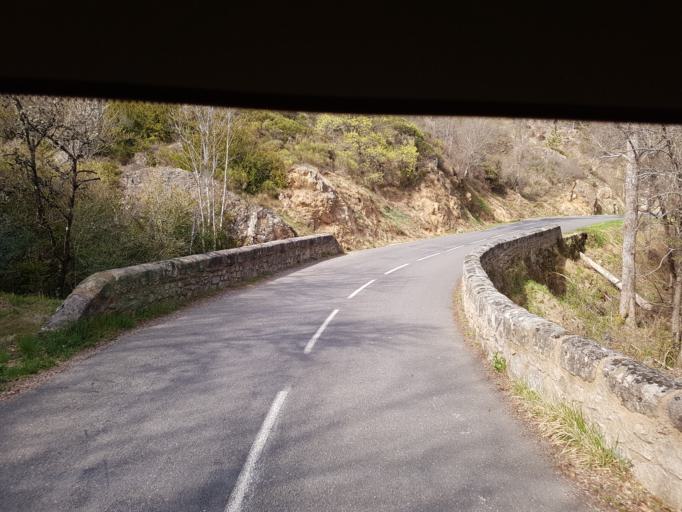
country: FR
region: Languedoc-Roussillon
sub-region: Departement de la Lozere
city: Florac
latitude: 44.3578
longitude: 3.6417
